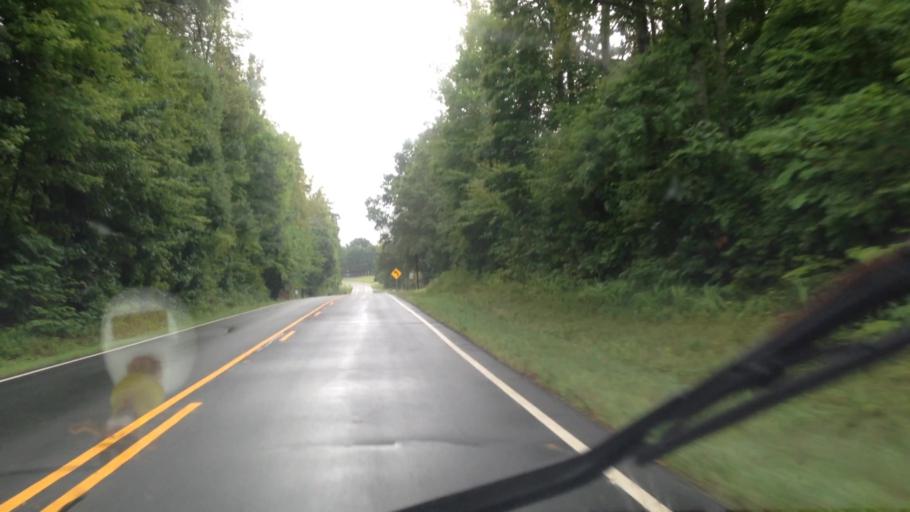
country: US
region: North Carolina
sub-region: Stokes County
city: Walnut Cove
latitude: 36.3784
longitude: -80.0911
